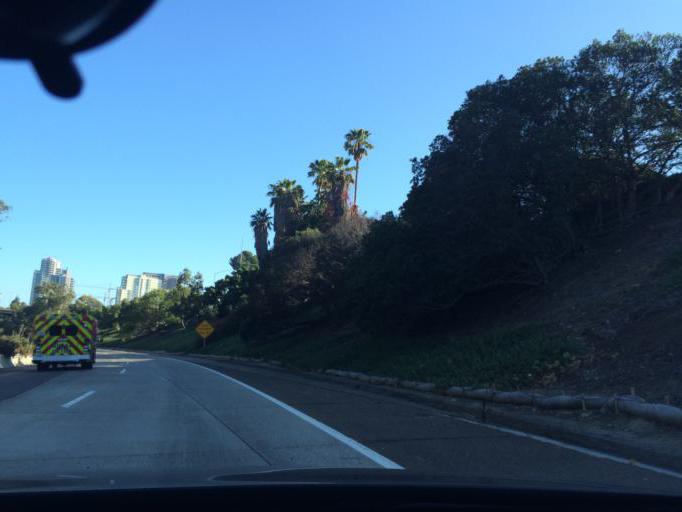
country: US
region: California
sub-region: San Diego County
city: San Diego
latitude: 32.7277
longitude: -117.1559
